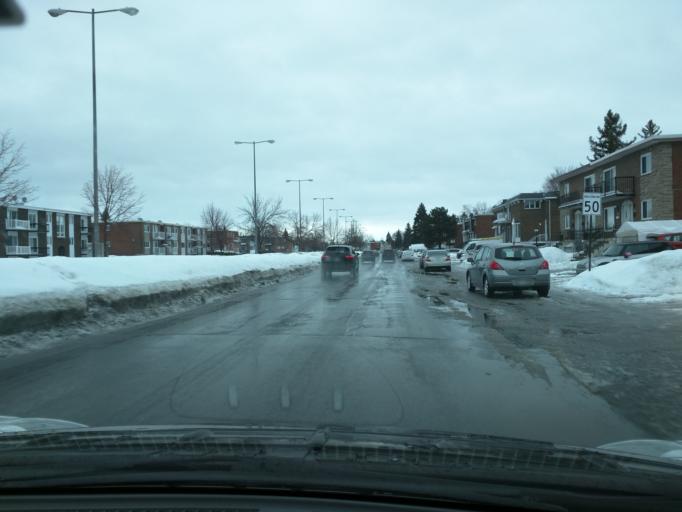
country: CA
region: Quebec
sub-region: Monteregie
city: Longueuil
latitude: 45.5160
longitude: -73.4656
